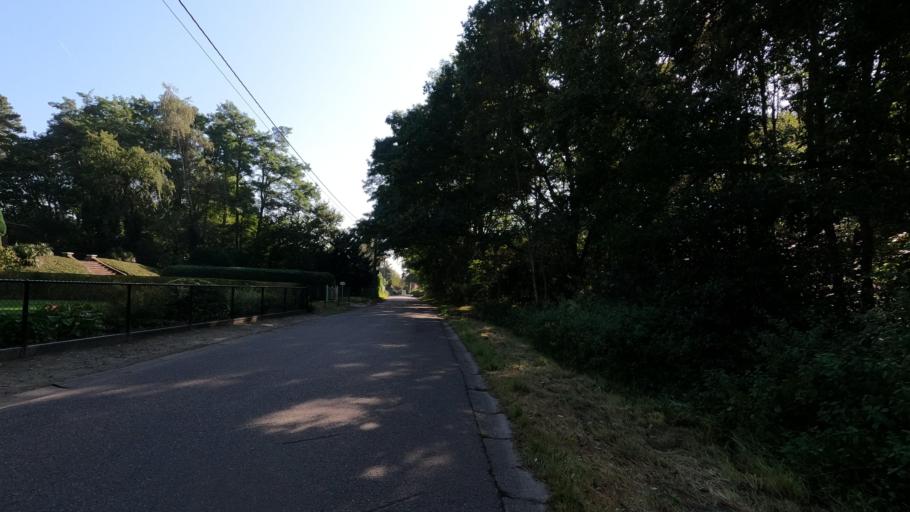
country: BE
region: Flanders
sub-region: Provincie Vlaams-Brabant
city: Haacht
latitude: 50.9939
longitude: 4.6704
